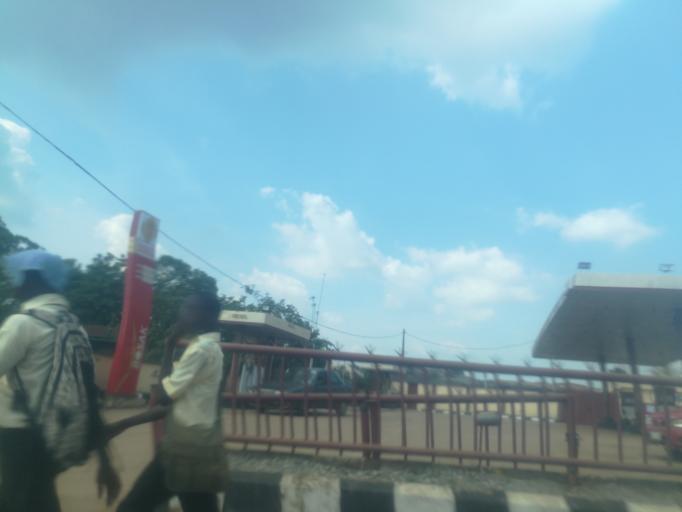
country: NG
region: Ogun
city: Abeokuta
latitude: 7.1712
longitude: 3.3670
